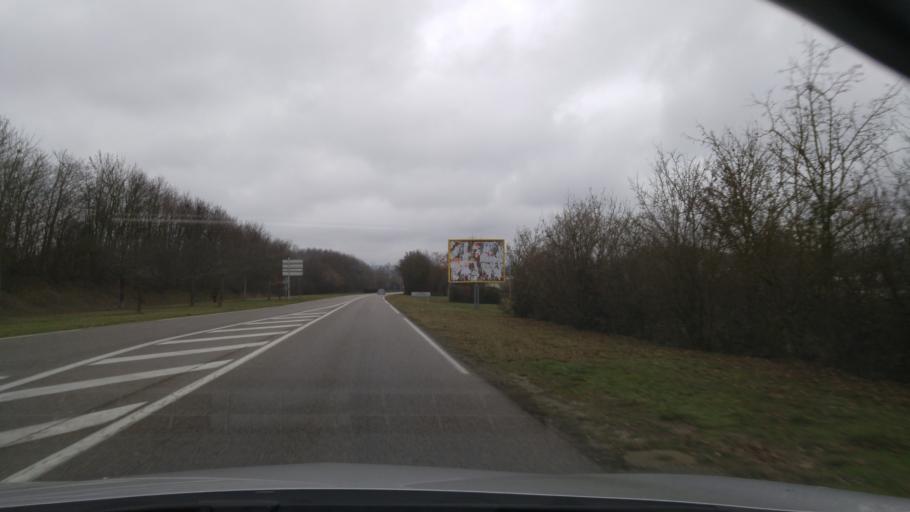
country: FR
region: Rhone-Alpes
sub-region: Departement de l'Isere
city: Villefontaine
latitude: 45.6212
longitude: 5.1424
